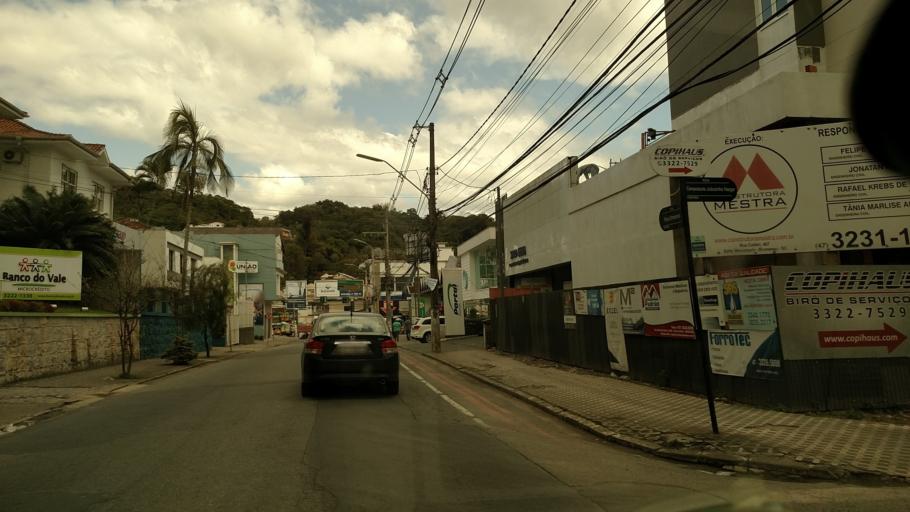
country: BR
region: Santa Catarina
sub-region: Blumenau
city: Blumenau
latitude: -26.9153
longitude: -49.0712
